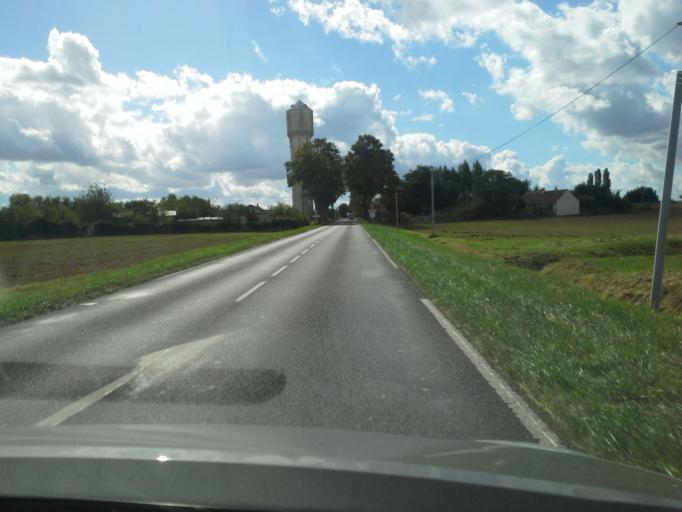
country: FR
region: Centre
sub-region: Departement du Loir-et-Cher
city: Pontlevoy
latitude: 47.4001
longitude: 1.2627
